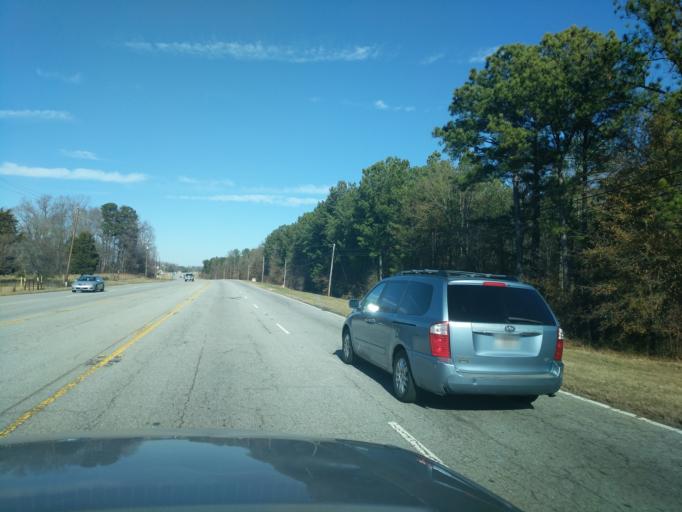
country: US
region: South Carolina
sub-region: Spartanburg County
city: Mayo
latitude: 35.0975
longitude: -81.8549
